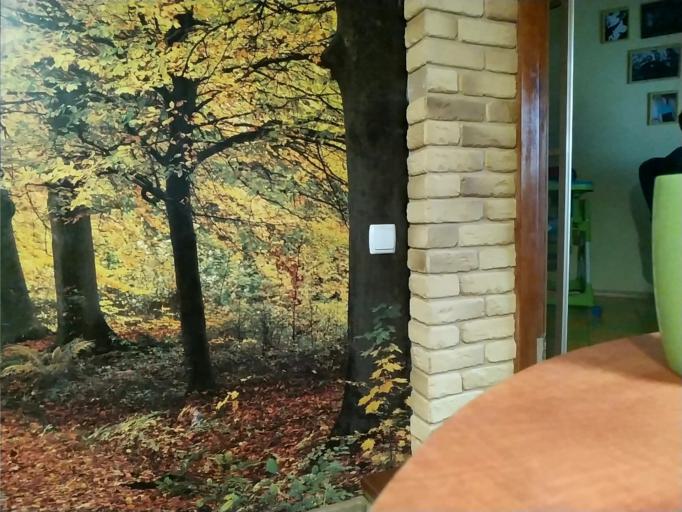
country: RU
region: Tverskaya
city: Staraya Toropa
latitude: 56.3461
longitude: 31.8318
